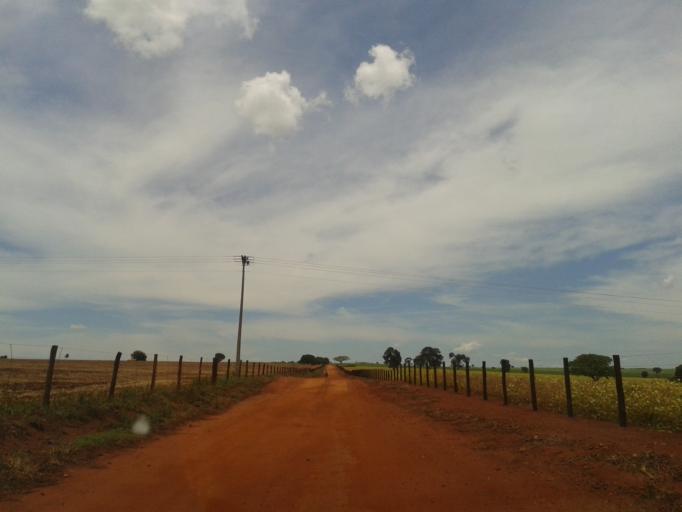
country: BR
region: Minas Gerais
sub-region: Capinopolis
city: Capinopolis
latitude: -18.7024
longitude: -49.7124
